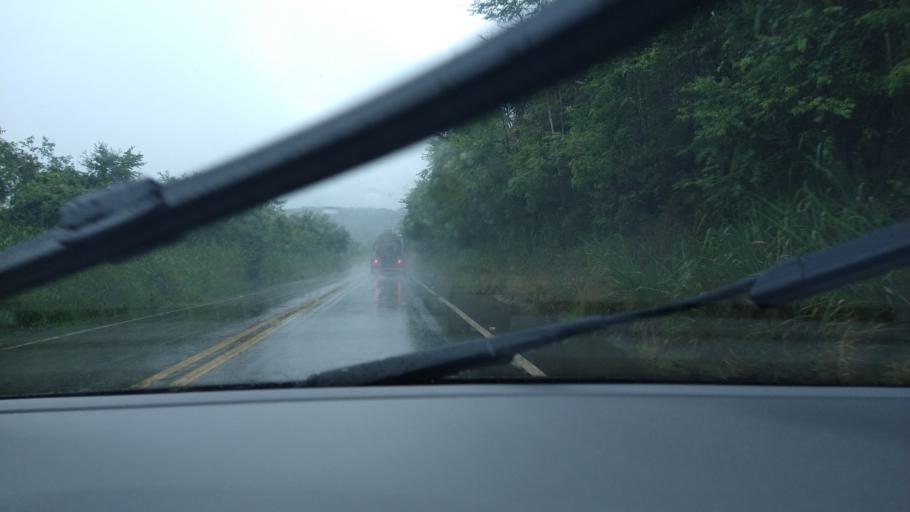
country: BR
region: Minas Gerais
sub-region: Ponte Nova
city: Ponte Nova
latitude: -20.5427
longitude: -42.8873
